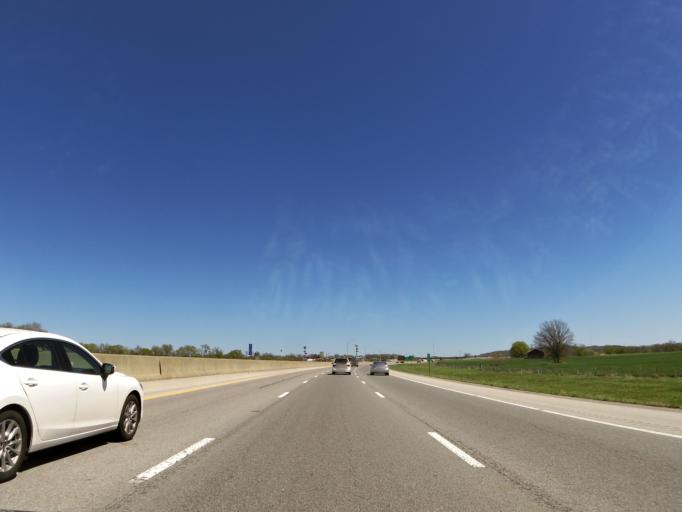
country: US
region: Kentucky
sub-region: Edmonson County
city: Brownsville
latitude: 37.0416
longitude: -86.2194
